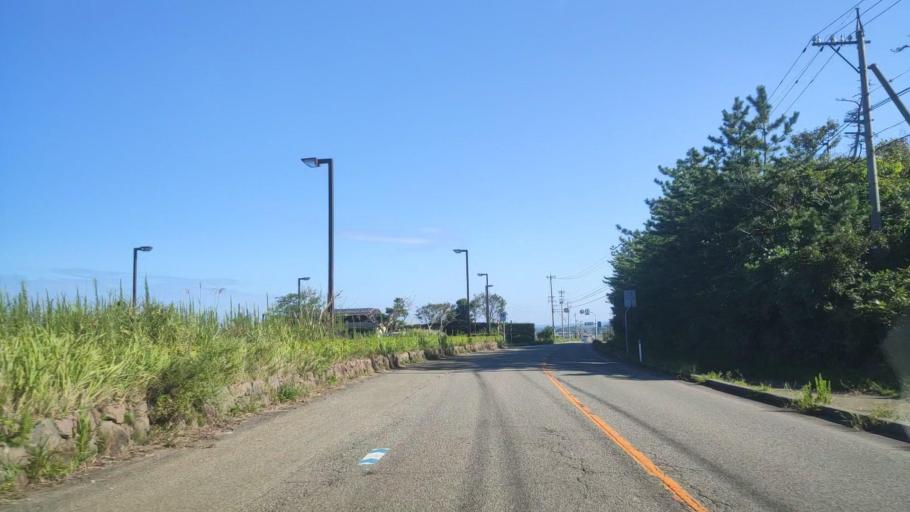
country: JP
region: Ishikawa
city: Hakui
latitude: 36.9328
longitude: 136.7563
